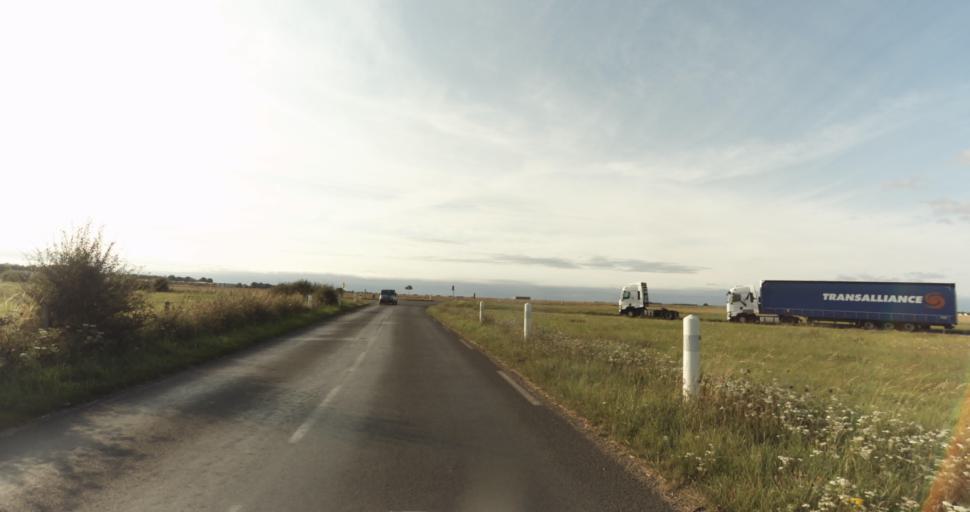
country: FR
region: Haute-Normandie
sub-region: Departement de l'Eure
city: Marcilly-sur-Eure
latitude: 48.8845
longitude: 1.2632
